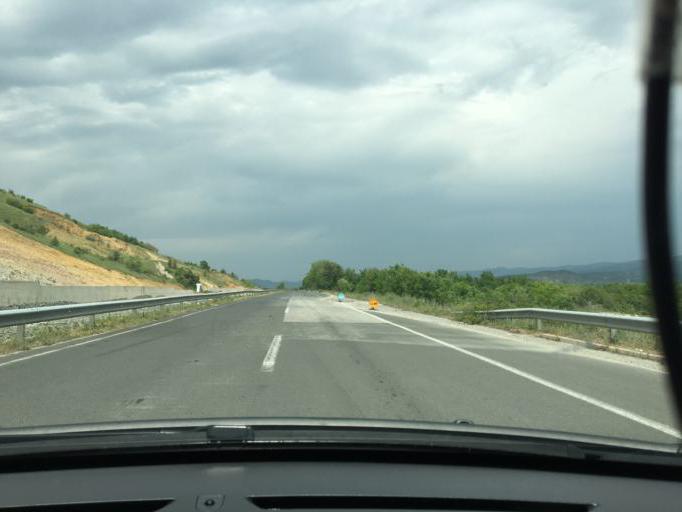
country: MK
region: Demir Kapija
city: Demir Kapija
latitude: 41.4404
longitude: 22.1808
